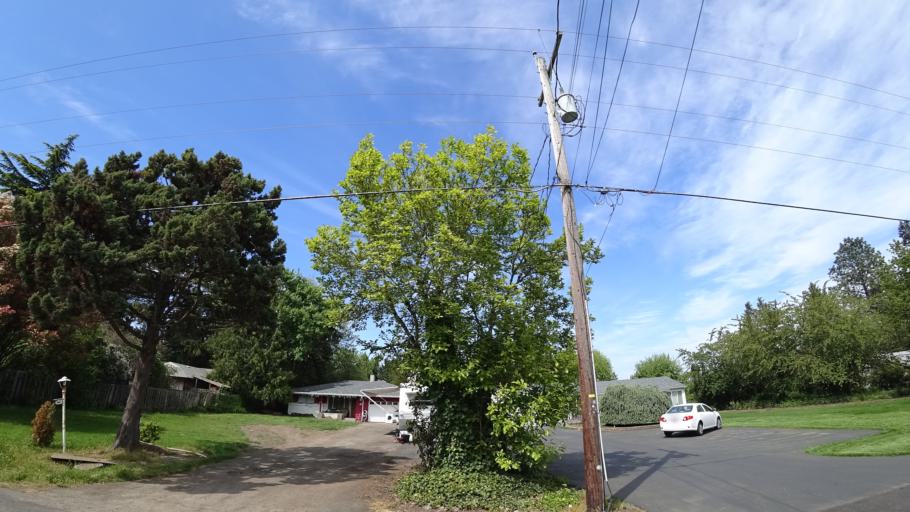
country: US
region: Oregon
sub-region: Washington County
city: Aloha
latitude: 45.4891
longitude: -122.8840
